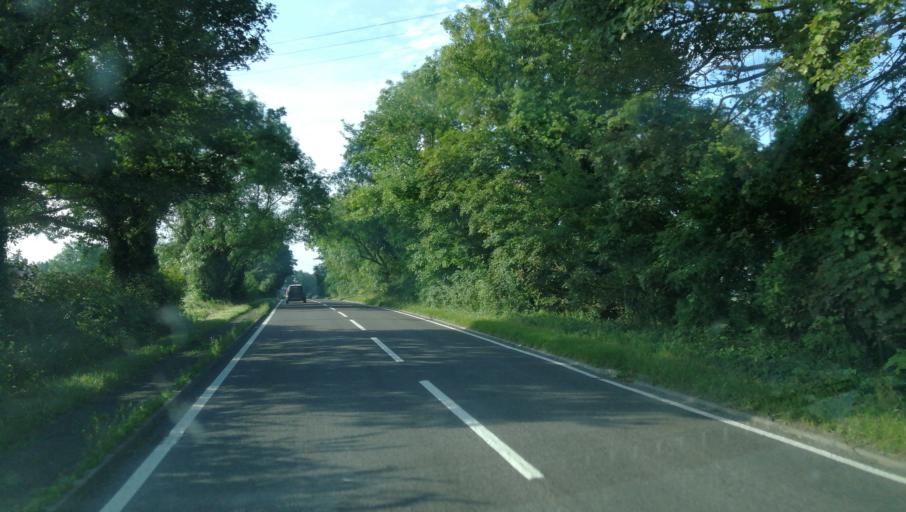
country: GB
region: England
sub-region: Oxfordshire
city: Deddington
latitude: 51.9250
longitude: -1.3249
